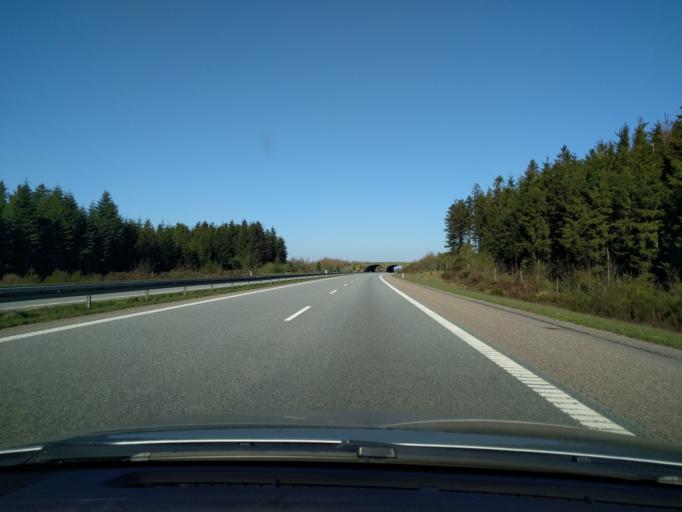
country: DK
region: South Denmark
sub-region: Vejle Kommune
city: Give
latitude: 55.8359
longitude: 9.2963
